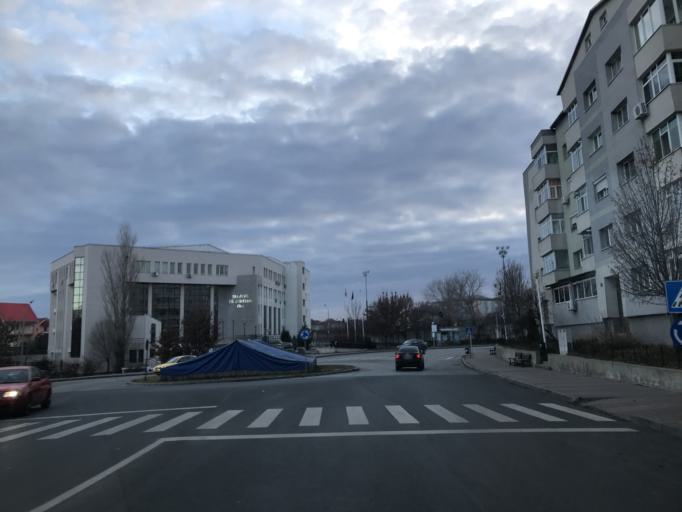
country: RO
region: Olt
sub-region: Municipiul Slatina
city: Slatina
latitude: 44.4251
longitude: 24.3717
